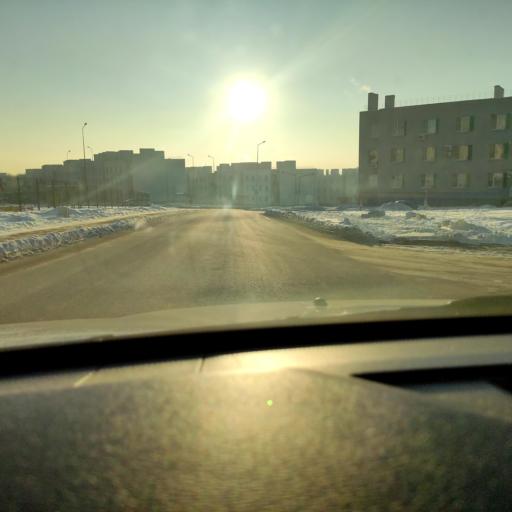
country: RU
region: Samara
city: Petra-Dubrava
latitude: 53.3044
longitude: 50.3426
